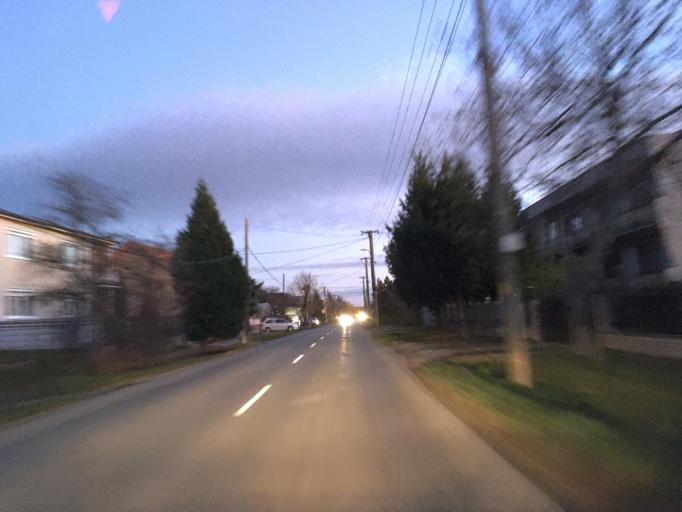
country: SK
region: Nitriansky
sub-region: Okres Nove Zamky
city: Nove Zamky
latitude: 47.9229
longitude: 18.1296
